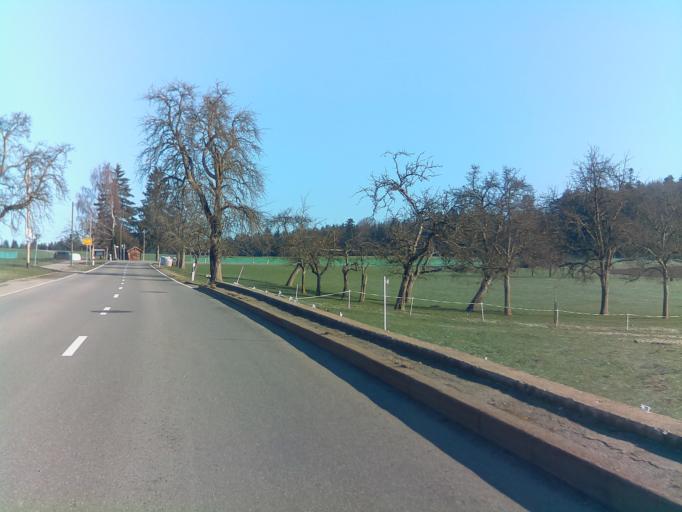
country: DE
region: Baden-Wuerttemberg
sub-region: Karlsruhe Region
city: Neuweiler
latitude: 48.6970
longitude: 8.5917
